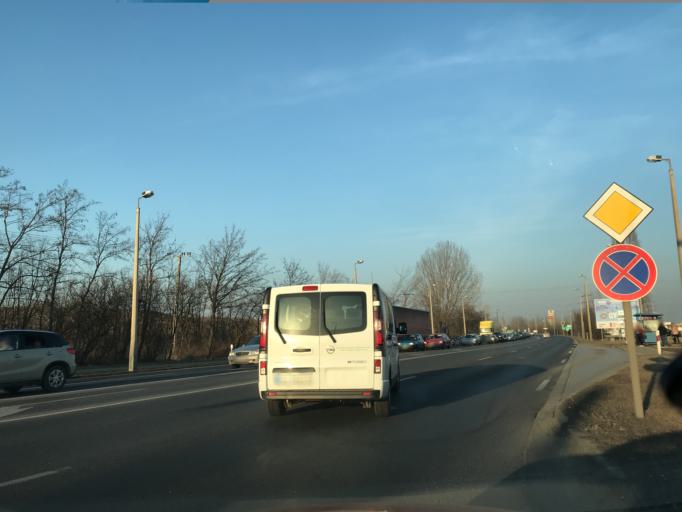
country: HU
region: Gyor-Moson-Sopron
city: Gyor
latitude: 47.6508
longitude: 17.6274
